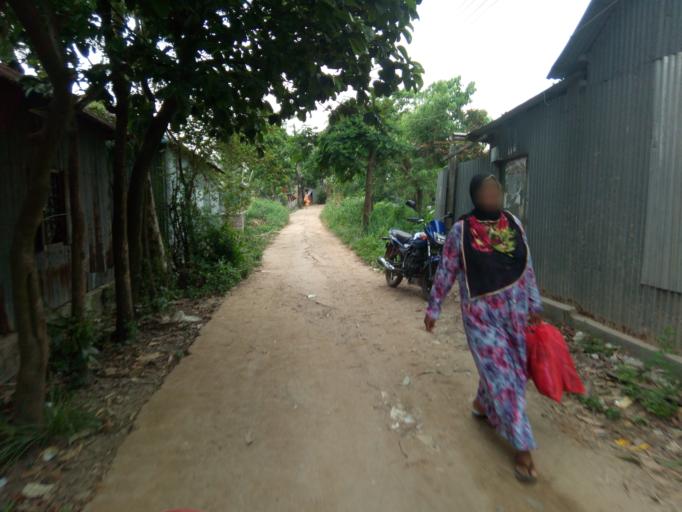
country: BD
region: Dhaka
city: Paltan
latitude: 23.7390
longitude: 90.4608
